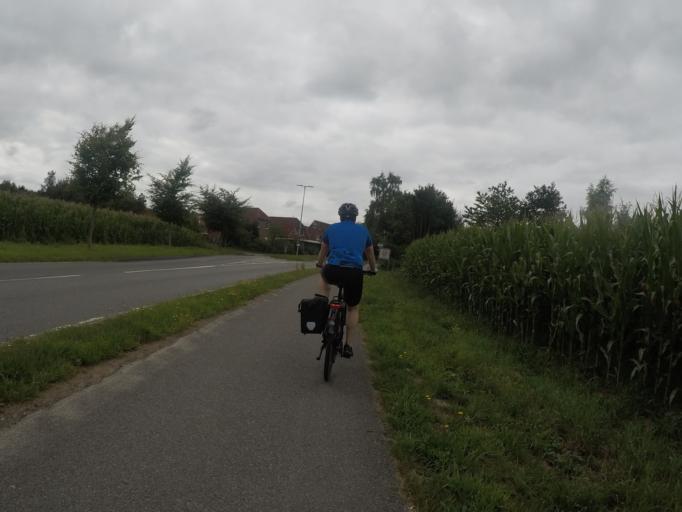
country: DE
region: Lower Saxony
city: Hammah
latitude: 53.5985
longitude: 9.4172
